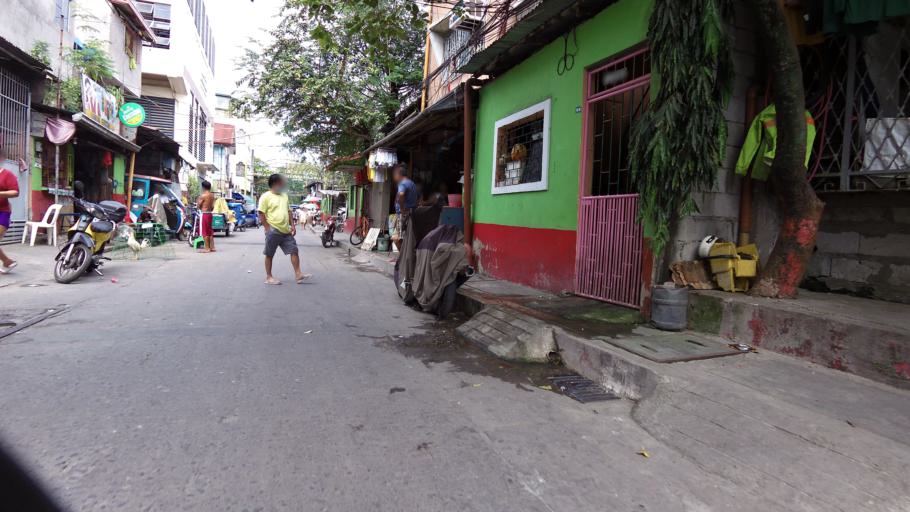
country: PH
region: Calabarzon
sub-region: Province of Rizal
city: Pateros
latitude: 14.5609
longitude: 121.0877
